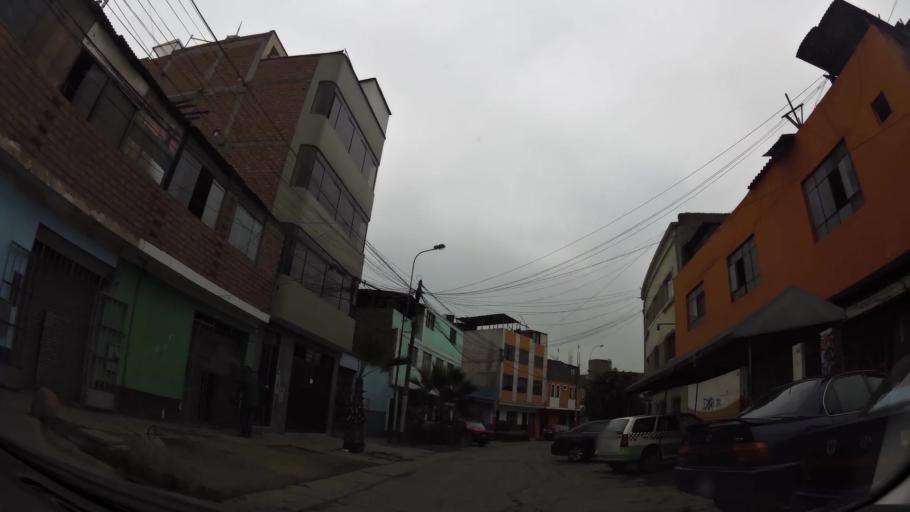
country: PE
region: Lima
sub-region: Lima
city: San Luis
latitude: -12.0700
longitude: -77.0078
